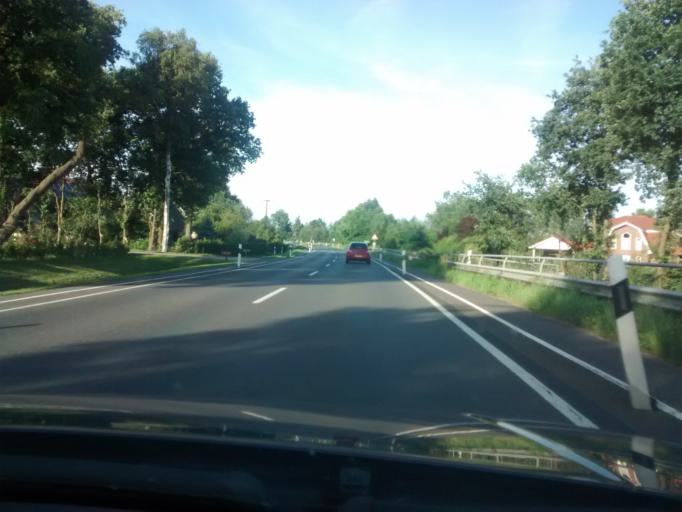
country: DE
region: Lower Saxony
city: Twist
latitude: 52.6474
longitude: 7.1237
